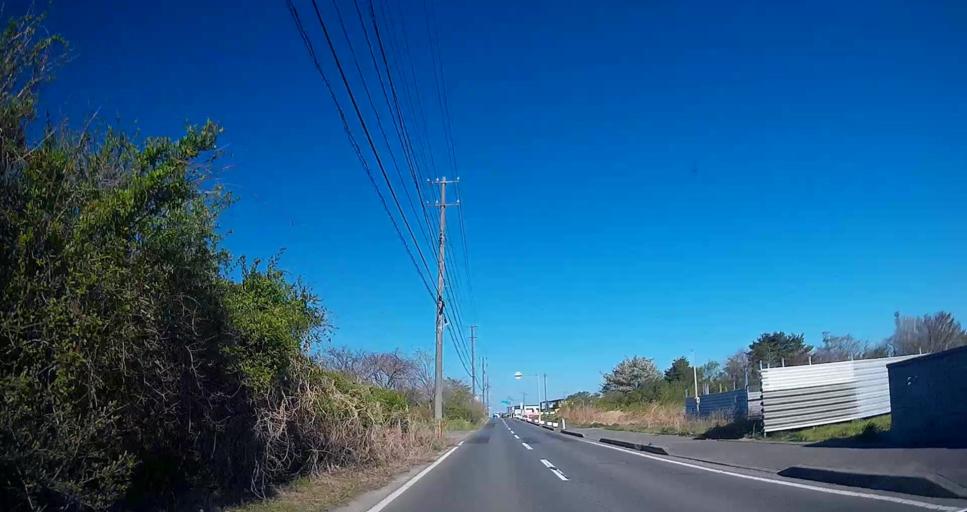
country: JP
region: Aomori
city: Hachinohe
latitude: 40.5214
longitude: 141.5670
